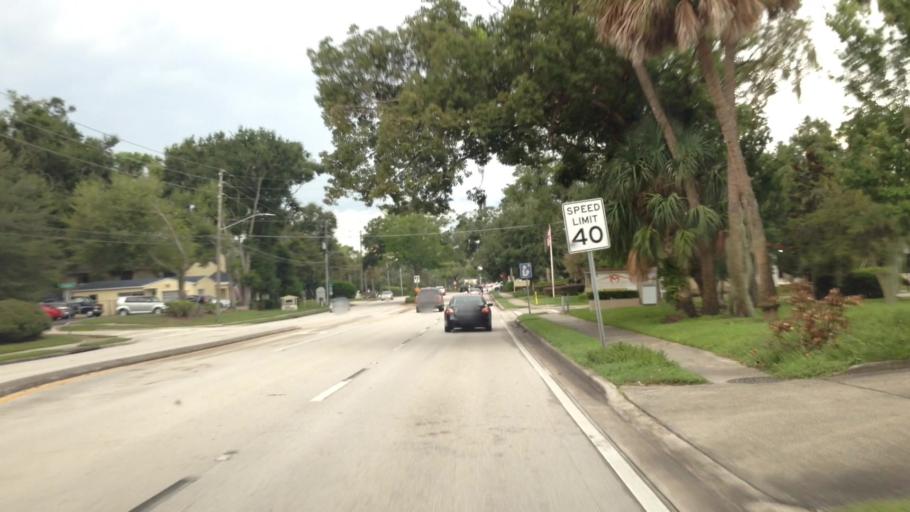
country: US
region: Florida
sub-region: Seminole County
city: Altamonte Springs
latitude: 28.6578
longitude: -81.3659
